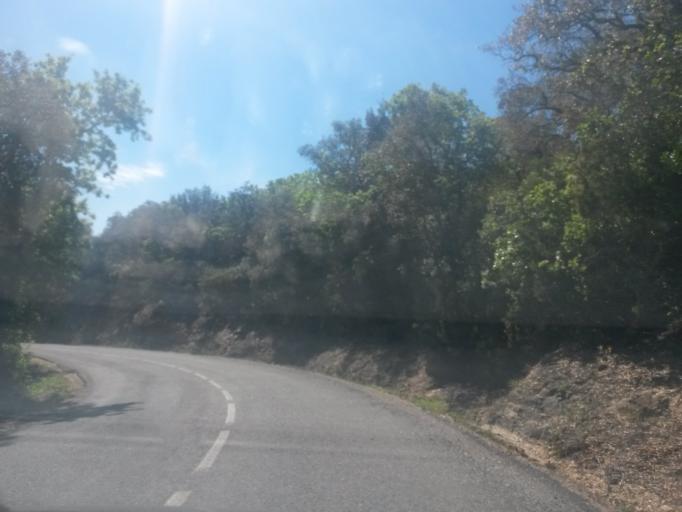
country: ES
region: Catalonia
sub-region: Provincia de Girona
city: Juia
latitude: 41.9833
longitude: 2.9231
